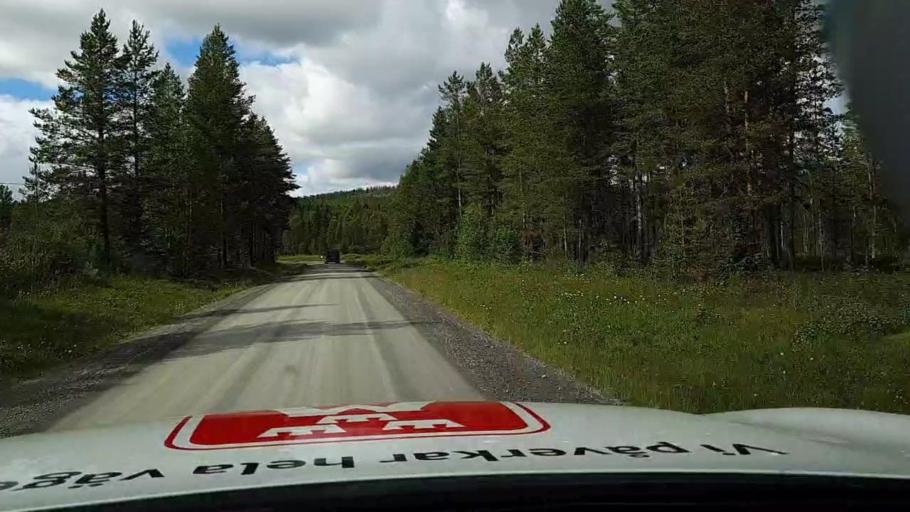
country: SE
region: Jaemtland
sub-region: Krokoms Kommun
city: Valla
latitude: 63.7059
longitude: 13.5918
